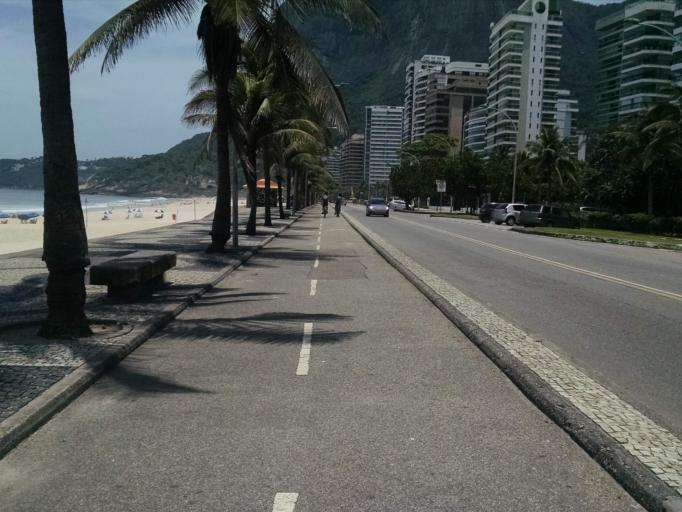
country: BR
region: Rio de Janeiro
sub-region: Rio De Janeiro
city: Rio de Janeiro
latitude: -22.9995
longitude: -43.2644
